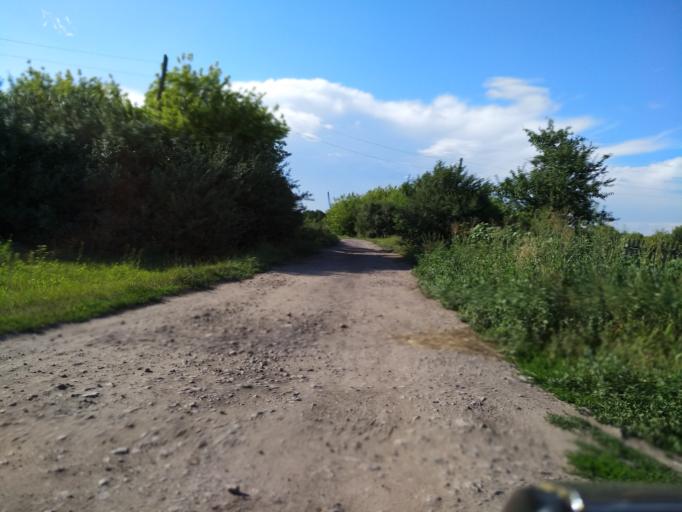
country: RU
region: Lipetsk
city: Dobrinka
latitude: 52.0327
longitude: 40.5628
